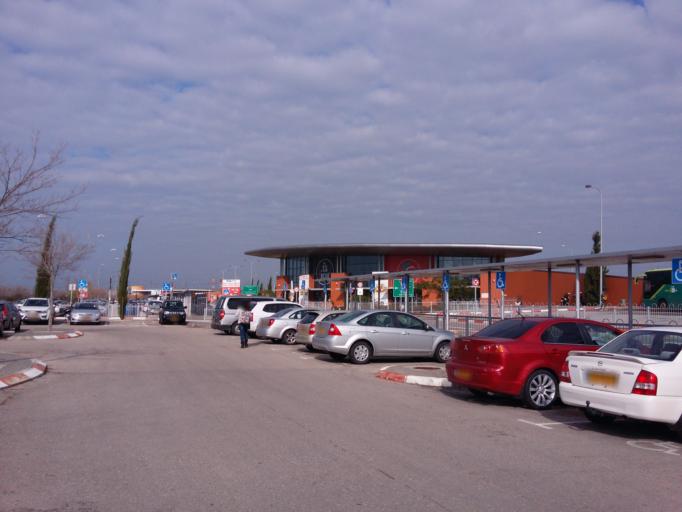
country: IL
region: Tel Aviv
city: Bene Beraq
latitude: 32.1100
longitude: 34.8386
